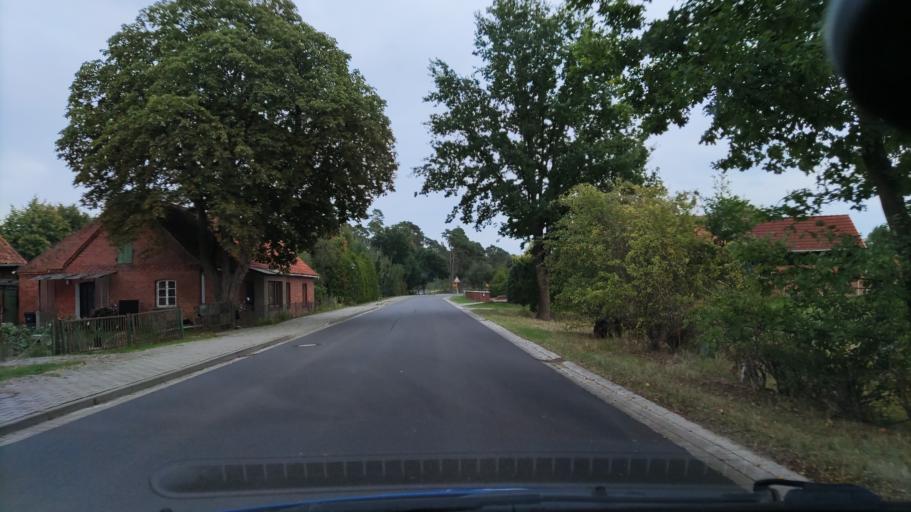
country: DE
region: Lower Saxony
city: Hitzacker
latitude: 53.2251
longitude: 10.9933
